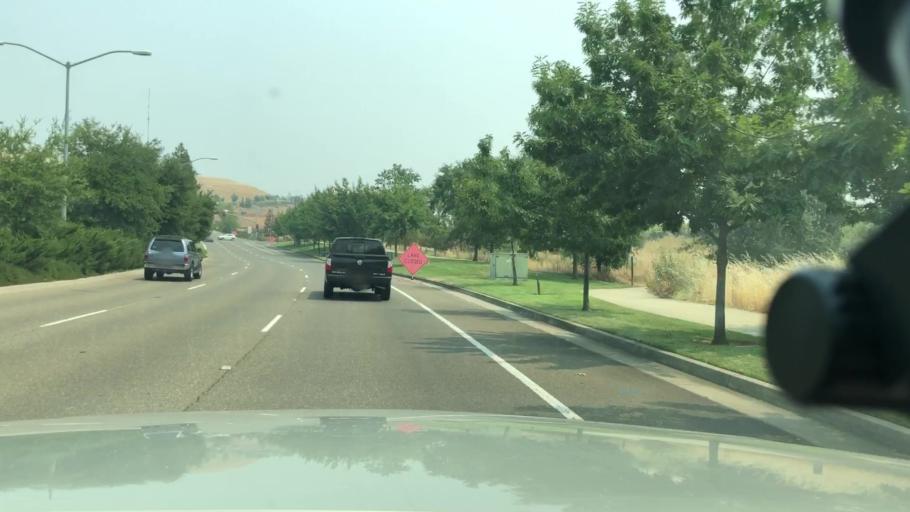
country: US
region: California
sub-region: El Dorado County
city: El Dorado Hills
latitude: 38.6478
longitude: -121.1096
